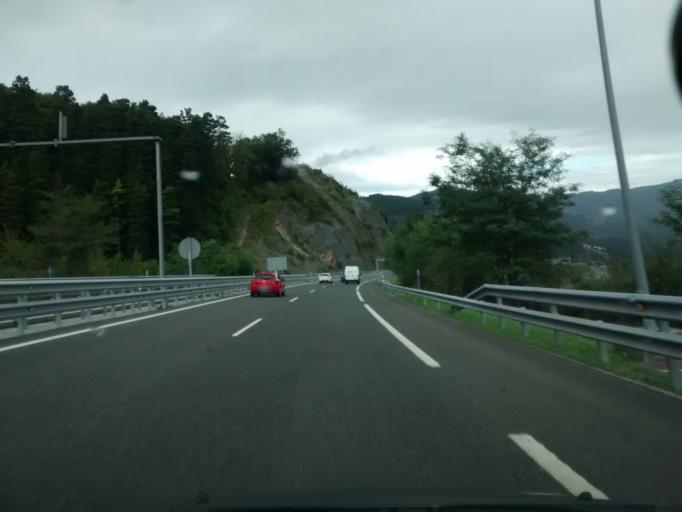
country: ES
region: Basque Country
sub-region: Provincia de Guipuzcoa
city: Bergara
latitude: 43.1219
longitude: -2.4285
